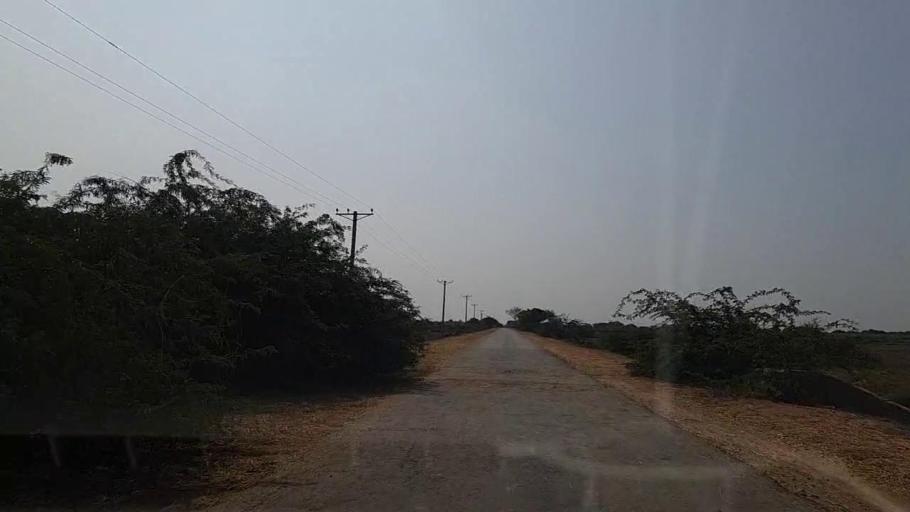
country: PK
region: Sindh
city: Chuhar Jamali
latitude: 24.2791
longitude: 67.9184
